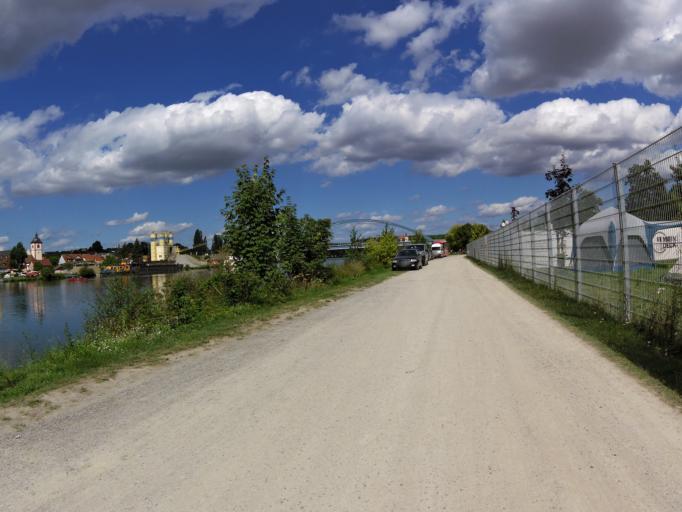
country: DE
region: Bavaria
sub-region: Regierungsbezirk Unterfranken
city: Volkach
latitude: 49.8617
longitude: 10.2222
